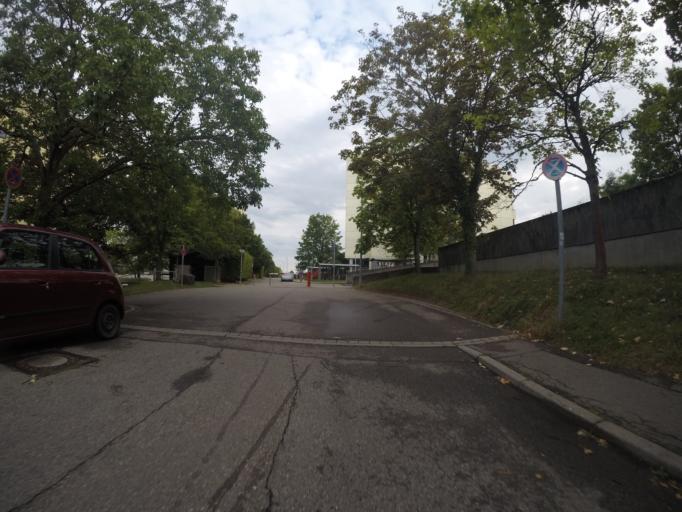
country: DE
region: Baden-Wuerttemberg
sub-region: Regierungsbezirk Stuttgart
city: Ostfildern
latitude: 48.7170
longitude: 9.2148
